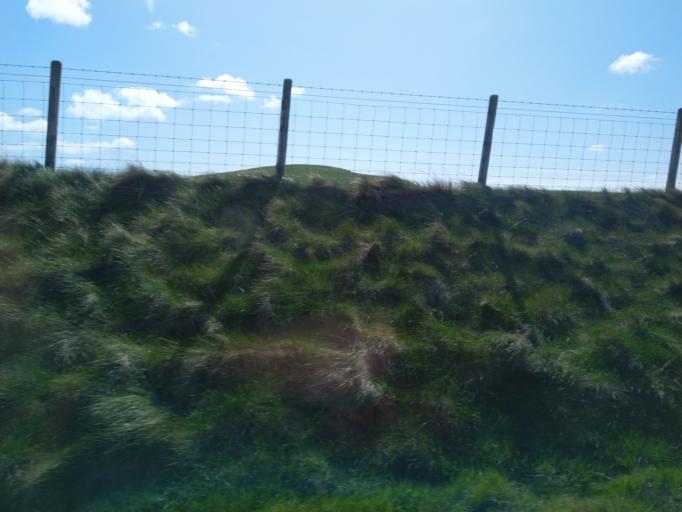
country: GB
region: Scotland
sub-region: Eilean Siar
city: Barra
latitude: 56.4847
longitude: -6.8928
